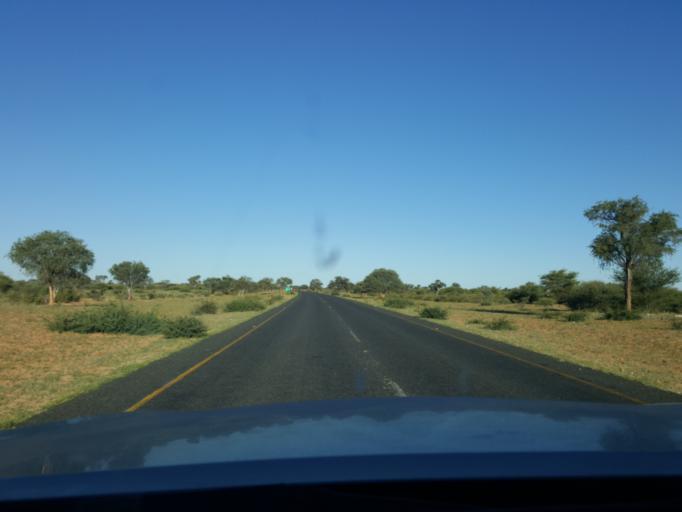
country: BW
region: Southern
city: Khakhea
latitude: -24.2314
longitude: 23.2488
